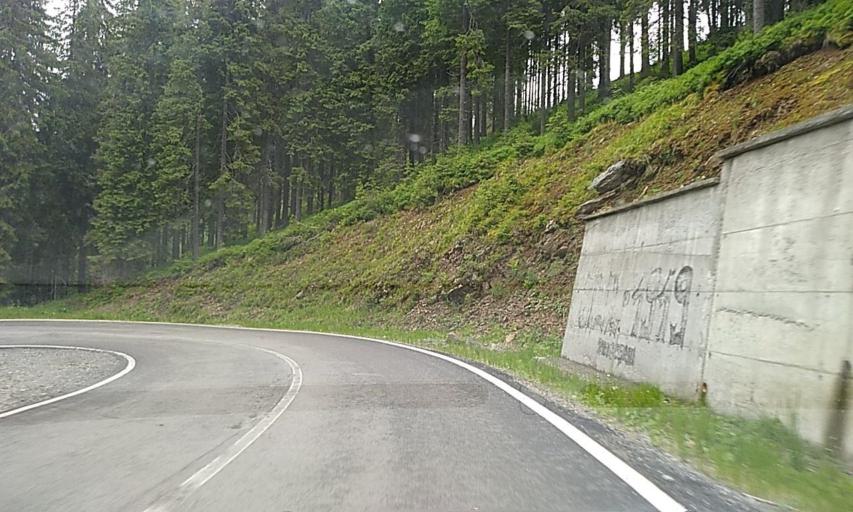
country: RO
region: Hunedoara
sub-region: Oras Petrila
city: Petrila
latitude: 45.4124
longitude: 23.6006
